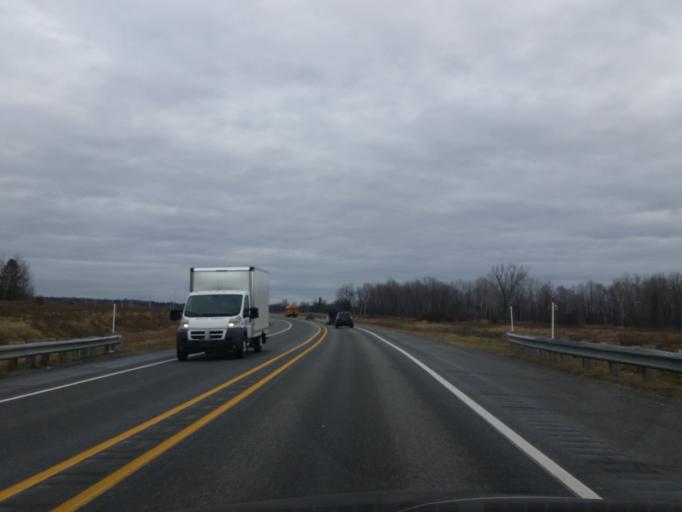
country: CA
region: Ontario
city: Clarence-Rockland
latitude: 45.5683
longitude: -75.3855
